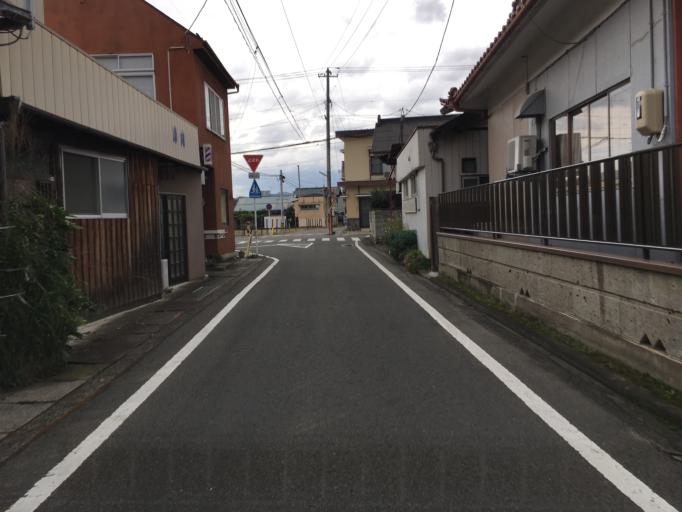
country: JP
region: Fukushima
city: Yanagawamachi-saiwaicho
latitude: 37.8559
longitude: 140.6089
